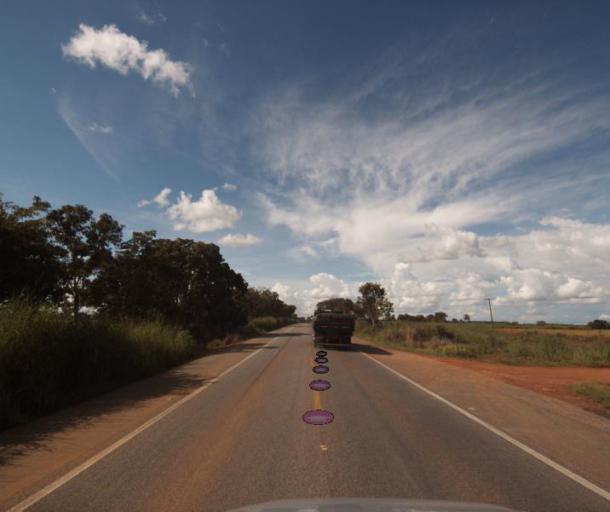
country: BR
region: Goias
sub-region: Porangatu
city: Porangatu
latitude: -13.0790
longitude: -49.1891
